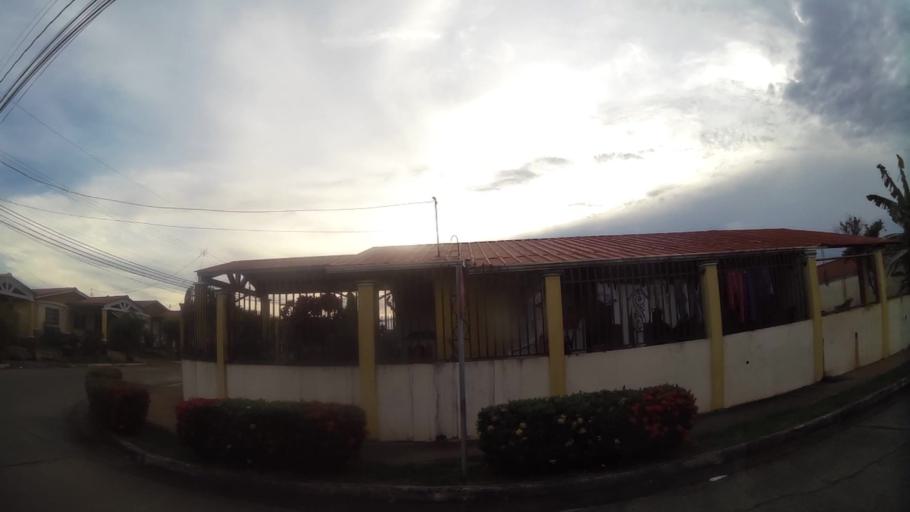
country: PA
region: Panama
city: La Chorrera
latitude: 8.8702
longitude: -79.7646
